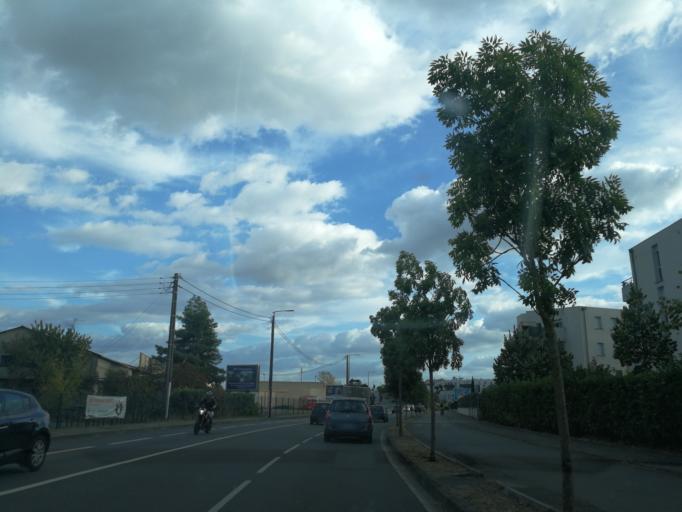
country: FR
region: Midi-Pyrenees
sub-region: Departement de la Haute-Garonne
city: L'Union
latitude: 43.6377
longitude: 1.4722
